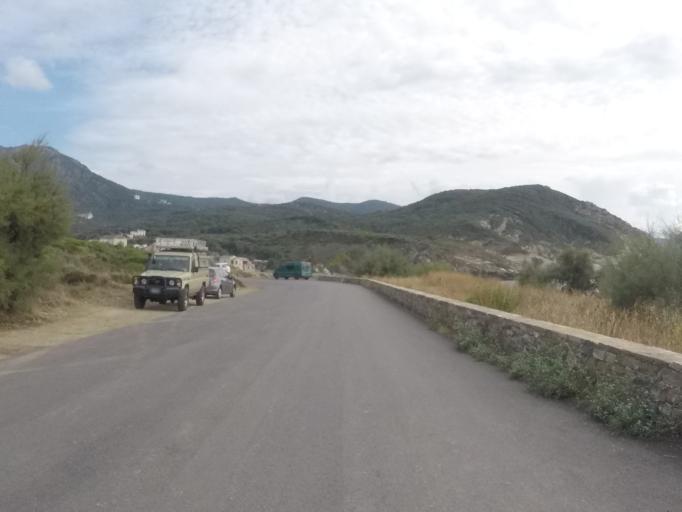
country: FR
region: Corsica
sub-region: Departement de la Haute-Corse
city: Brando
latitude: 42.9637
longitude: 9.3480
